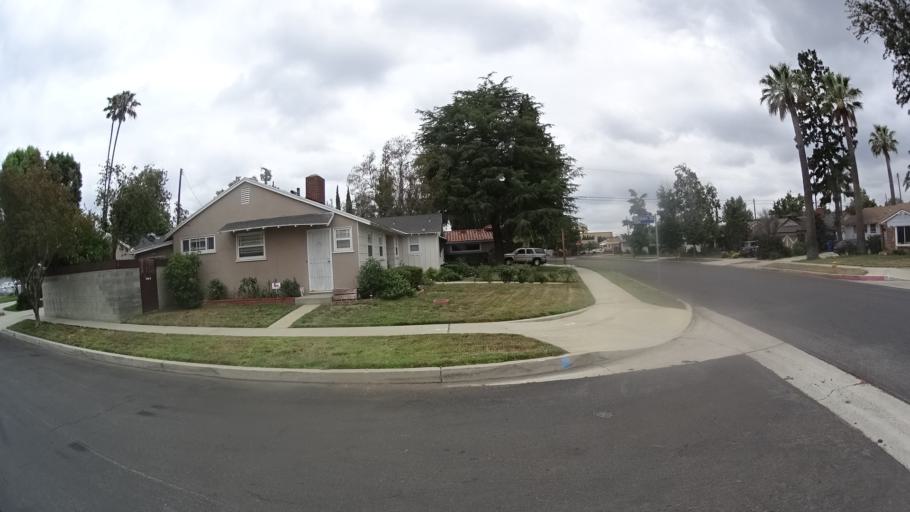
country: US
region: California
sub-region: Los Angeles County
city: San Fernando
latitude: 34.2618
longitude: -118.4659
